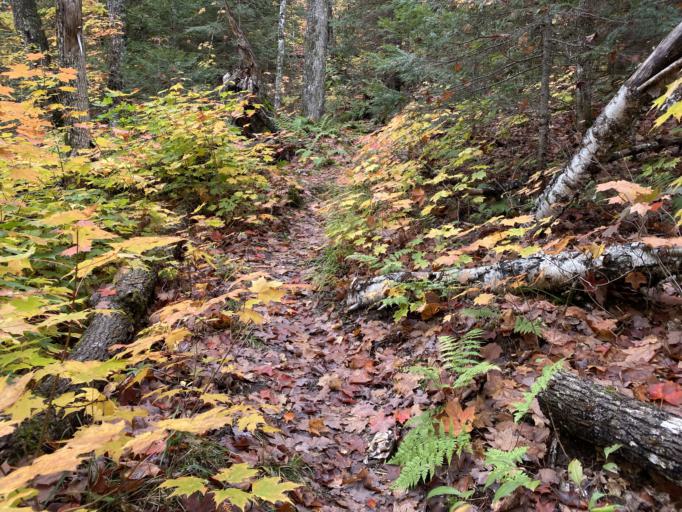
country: US
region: Michigan
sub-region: Marquette County
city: West Ishpeming
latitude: 46.5403
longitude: -87.9966
